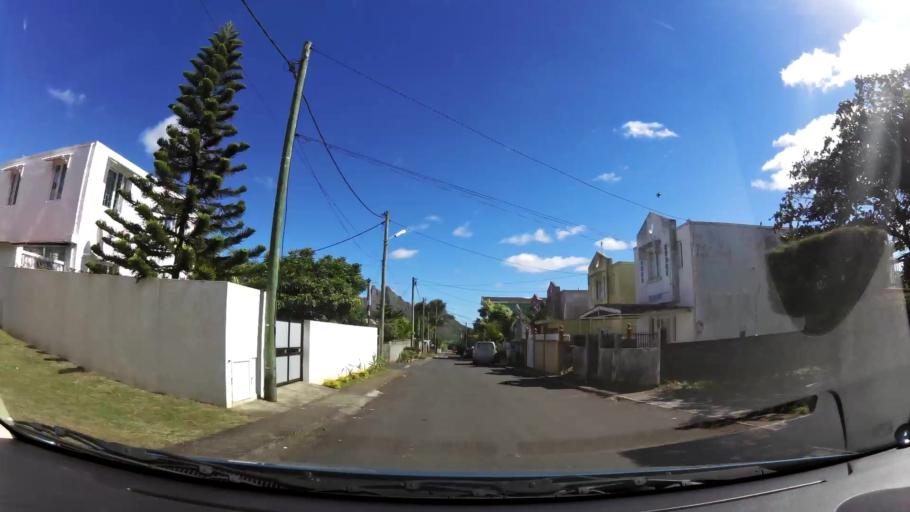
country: MU
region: Plaines Wilhems
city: Vacoas
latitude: -20.3050
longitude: 57.4736
